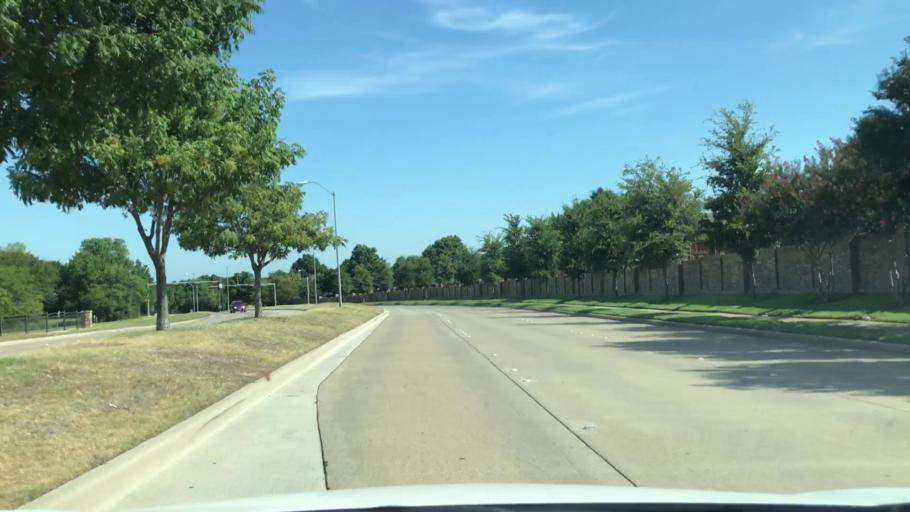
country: US
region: Texas
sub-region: Denton County
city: The Colony
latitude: 33.0597
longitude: -96.8386
